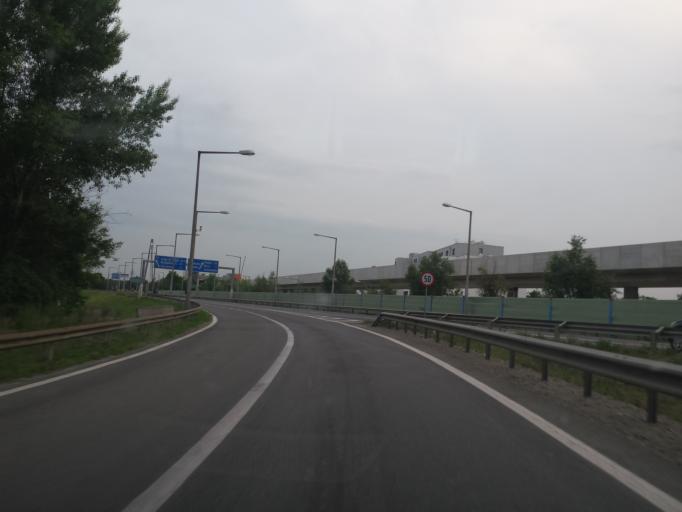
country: AT
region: Vienna
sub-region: Wien Stadt
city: Vienna
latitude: 48.2139
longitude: 16.4442
